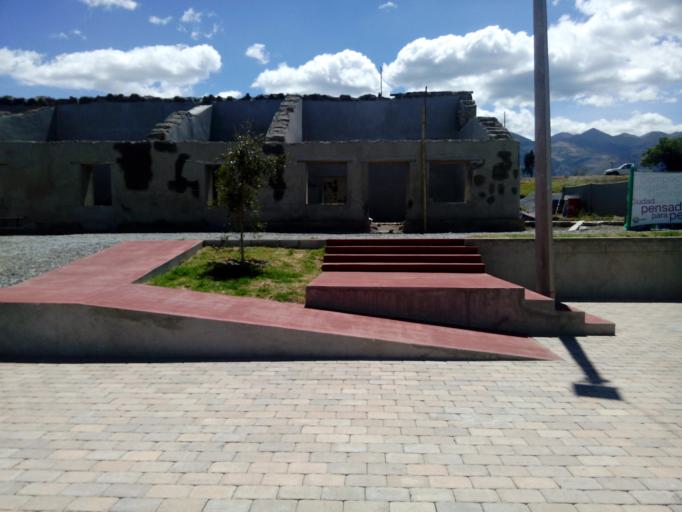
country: EC
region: Imbabura
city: Atuntaqui
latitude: 0.4194
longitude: -78.1901
